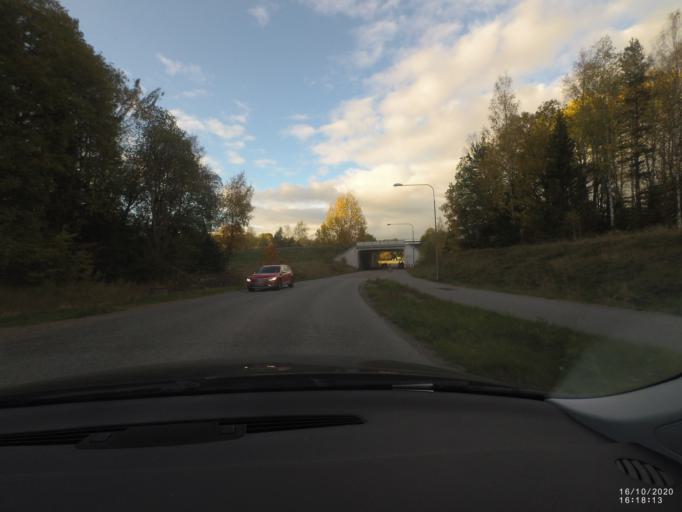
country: SE
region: Soedermanland
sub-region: Nykopings Kommun
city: Nykoping
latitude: 58.7691
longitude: 17.0074
